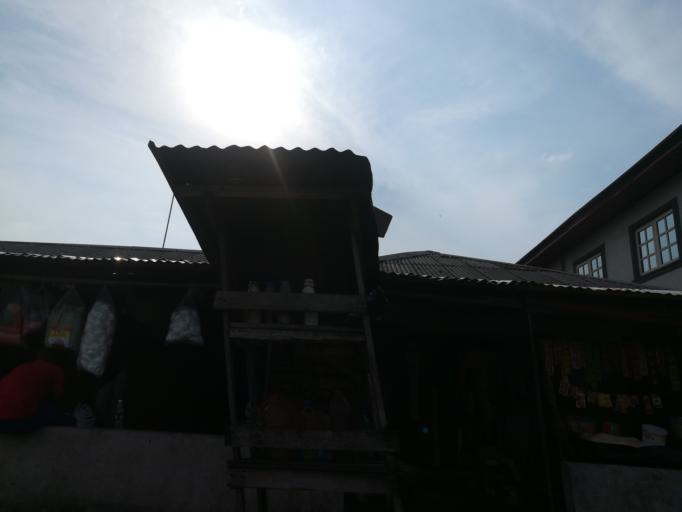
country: NG
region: Rivers
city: Okrika
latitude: 4.7327
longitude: 7.0844
